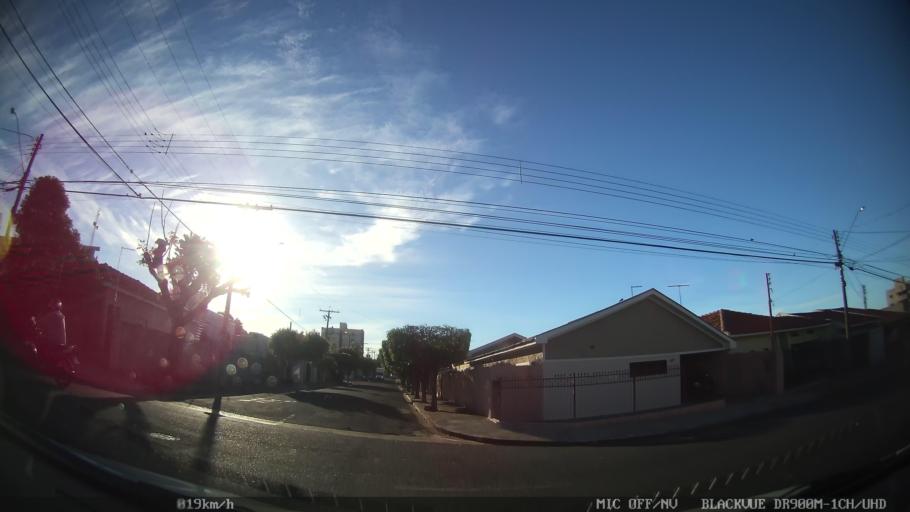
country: BR
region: Sao Paulo
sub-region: Sao Jose Do Rio Preto
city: Sao Jose do Rio Preto
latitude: -20.8307
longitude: -49.3706
